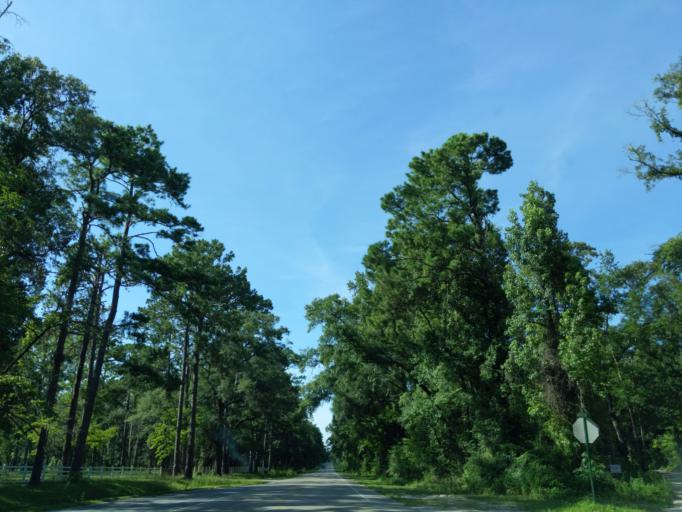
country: US
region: Florida
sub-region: Leon County
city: Woodville
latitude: 30.2756
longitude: -84.3125
